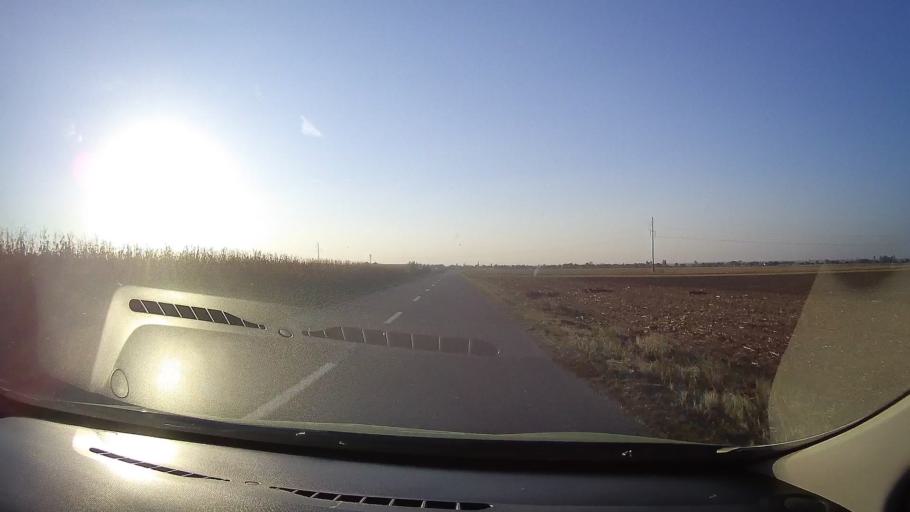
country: RO
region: Bihor
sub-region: Comuna Paleu
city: Paleu
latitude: 47.1619
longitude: 21.9636
